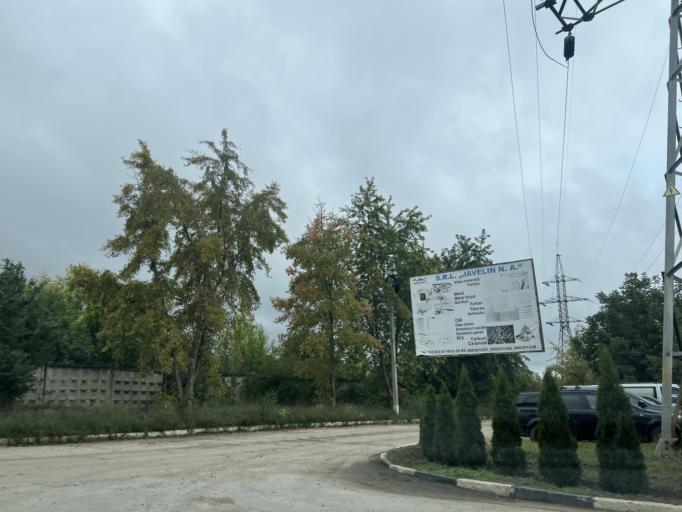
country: MD
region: Ungheni
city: Ungheni
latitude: 47.2261
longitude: 27.8050
